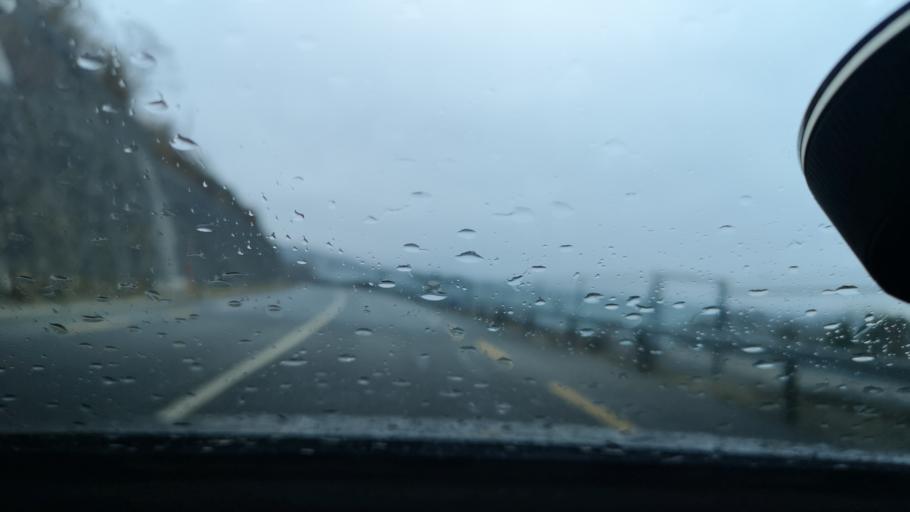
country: CH
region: Neuchatel
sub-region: Boudry District
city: Saint-Aubin-Sauges
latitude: 46.8668
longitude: 6.7511
